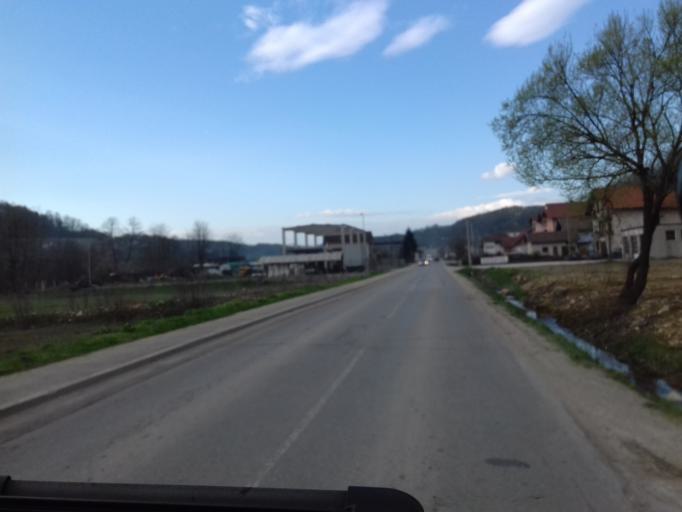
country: BA
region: Federation of Bosnia and Herzegovina
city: Tesanjka
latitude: 44.6431
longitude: 18.0191
